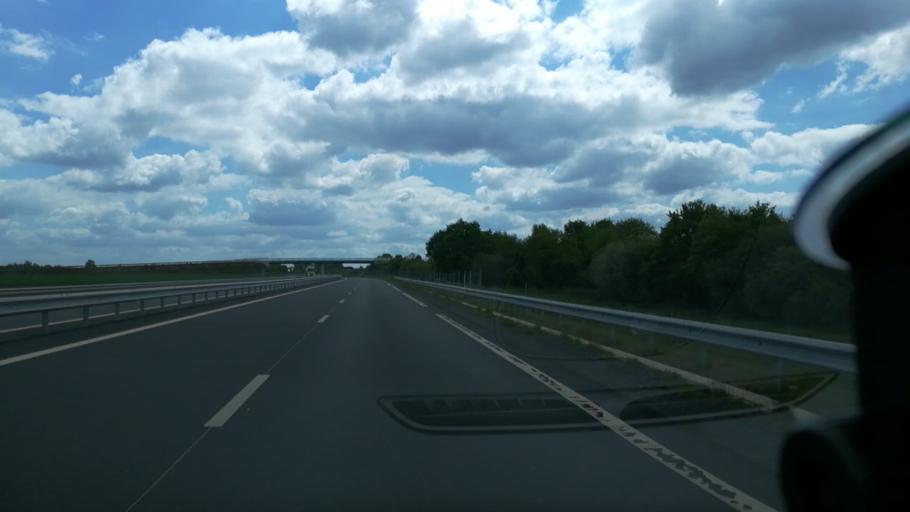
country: FR
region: Brittany
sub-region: Departement d'Ille-et-Vilaine
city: Retiers
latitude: 47.8756
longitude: -1.3631
